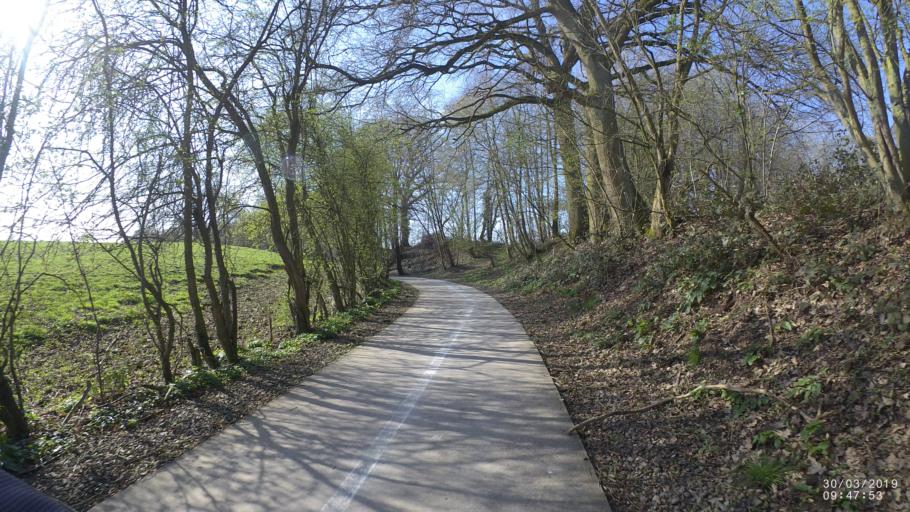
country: BE
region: Wallonia
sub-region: Province du Brabant Wallon
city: Louvain-la-Neuve
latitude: 50.6794
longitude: 4.6149
